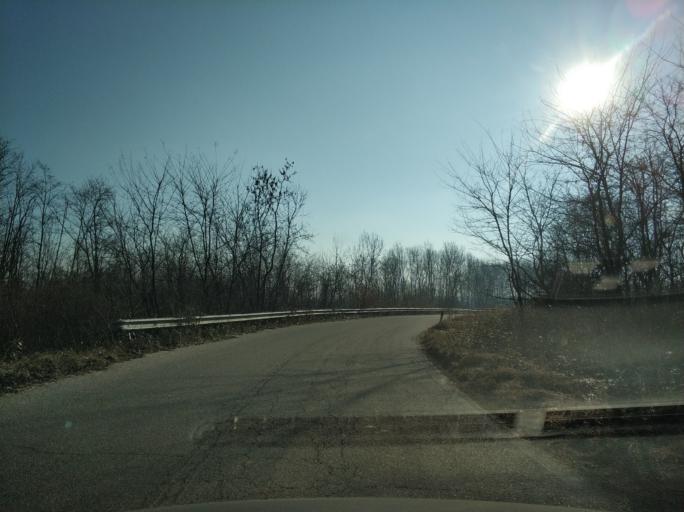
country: IT
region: Piedmont
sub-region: Provincia di Torino
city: Levone
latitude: 45.3077
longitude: 7.6151
